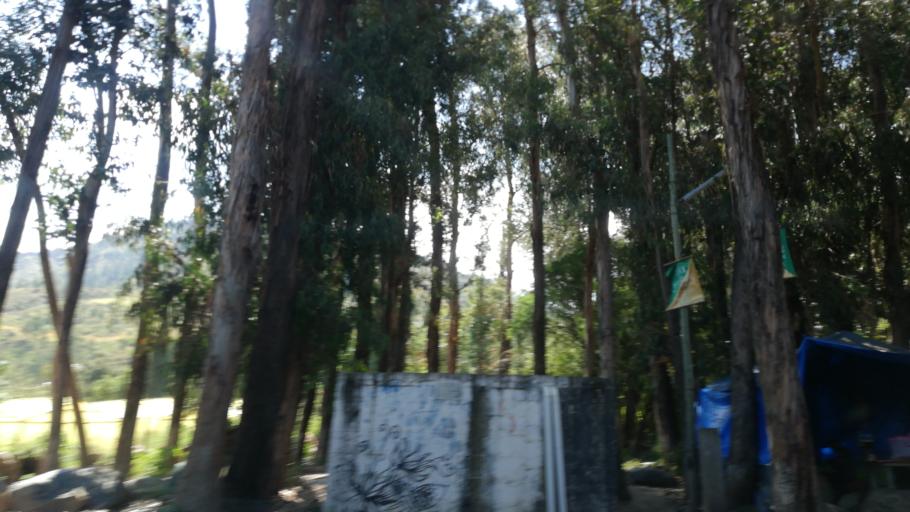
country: BO
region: Cochabamba
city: Cochabamba
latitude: -17.3215
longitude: -66.2123
